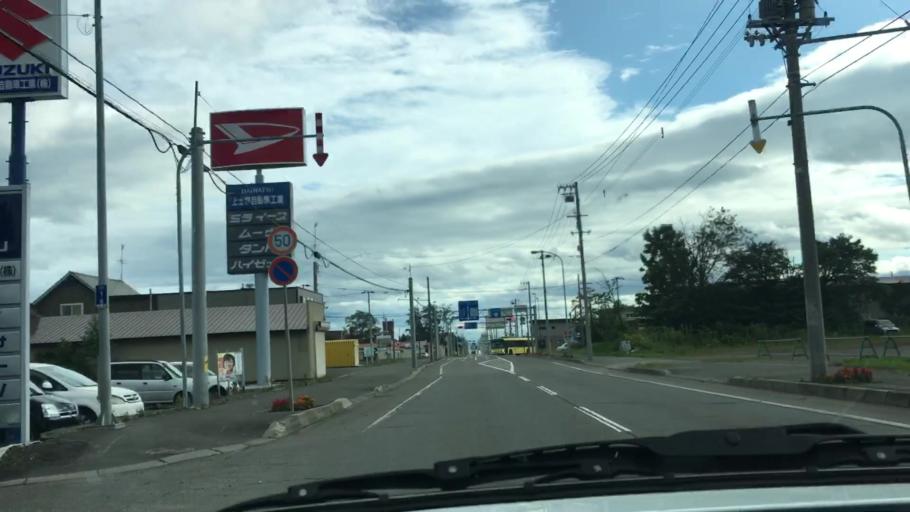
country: JP
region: Hokkaido
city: Otofuke
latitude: 43.2360
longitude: 143.2958
